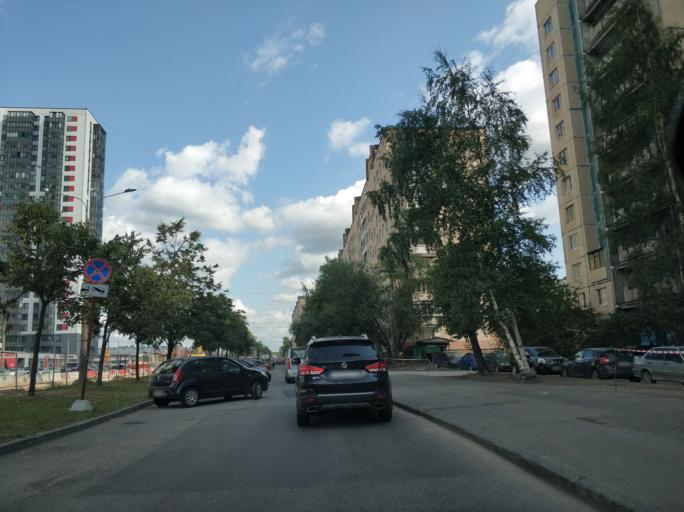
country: RU
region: St.-Petersburg
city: Krasnogvargeisky
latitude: 59.9591
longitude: 30.4800
